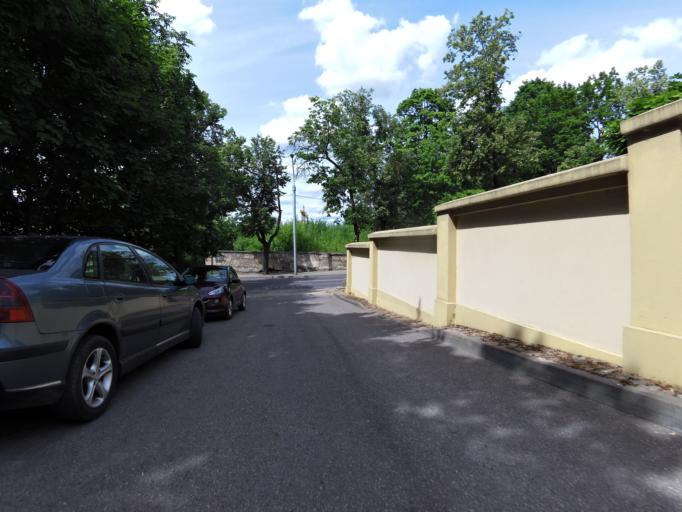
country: LT
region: Vilnius County
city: Rasos
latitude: 54.6748
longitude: 25.2951
